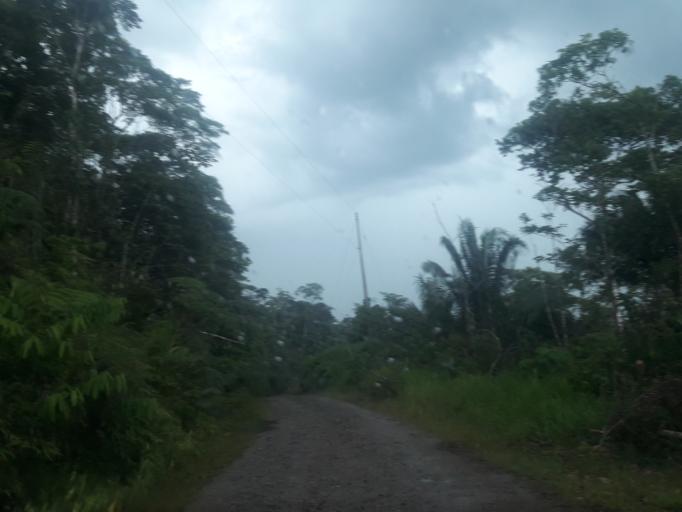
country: EC
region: Napo
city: Tena
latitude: -1.0895
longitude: -77.7058
